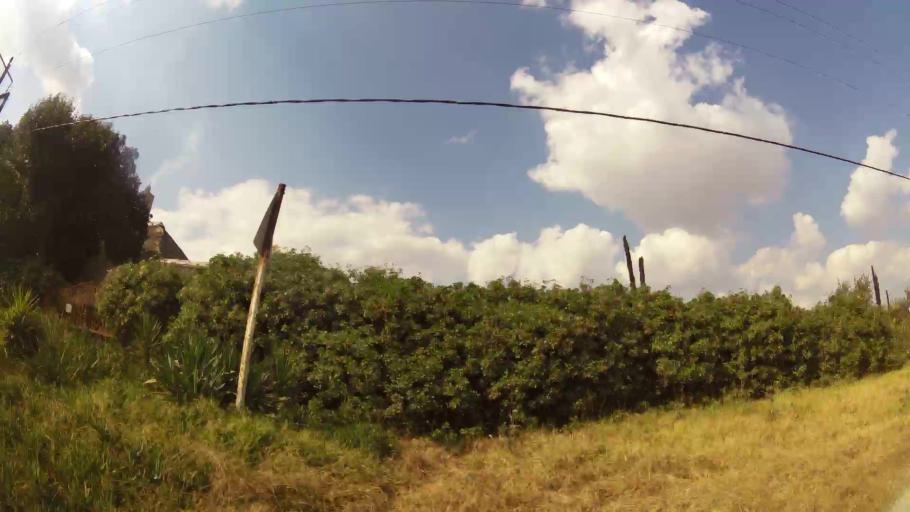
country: ZA
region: Mpumalanga
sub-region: Nkangala District Municipality
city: Delmas
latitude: -26.1503
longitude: 28.5452
